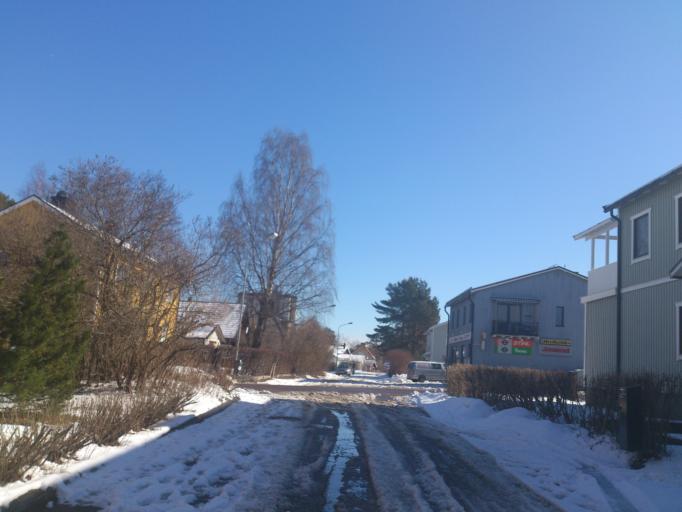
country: SE
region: Vaesternorrland
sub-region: Sundsvalls Kommun
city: Sundsvall
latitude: 62.3798
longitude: 17.3293
